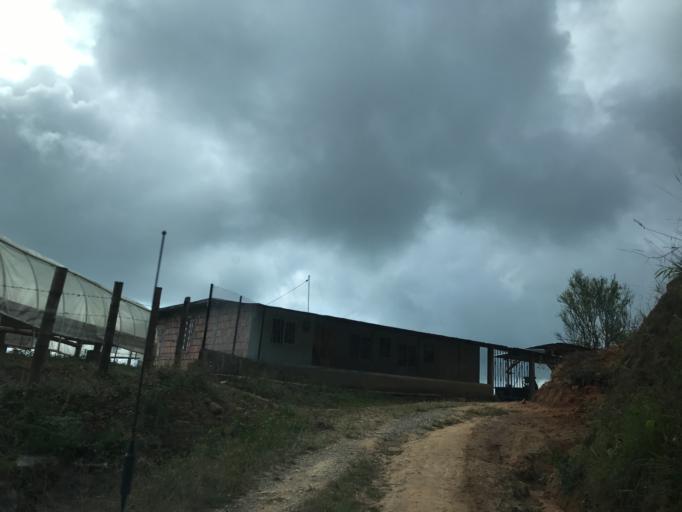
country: CO
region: Valle del Cauca
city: Obando
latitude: 4.5677
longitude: -75.8931
